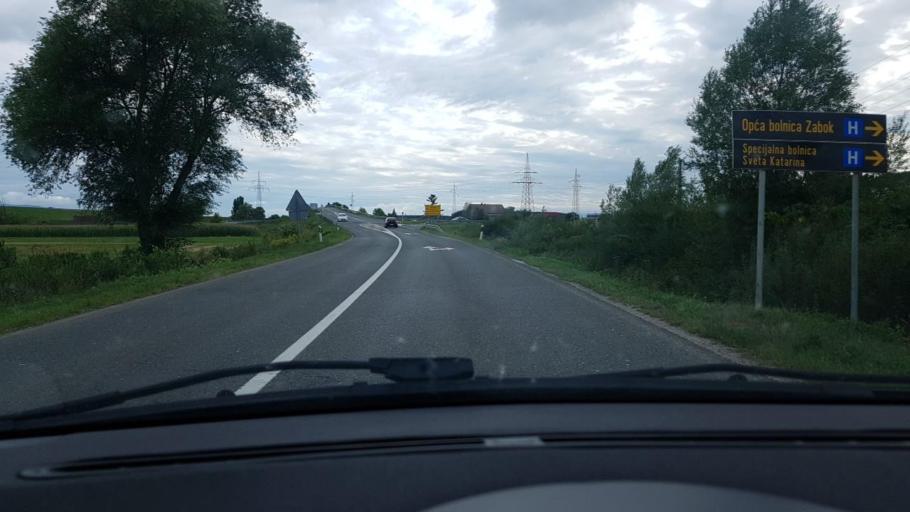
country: HR
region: Krapinsko-Zagorska
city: Zabok
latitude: 46.0285
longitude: 15.9138
